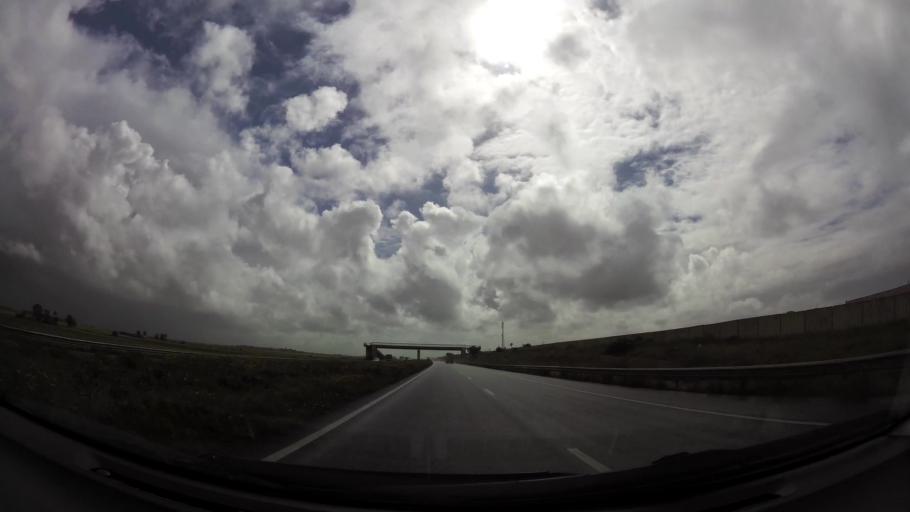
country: MA
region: Grand Casablanca
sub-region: Nouaceur
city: Dar Bouazza
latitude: 33.3846
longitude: -7.8897
